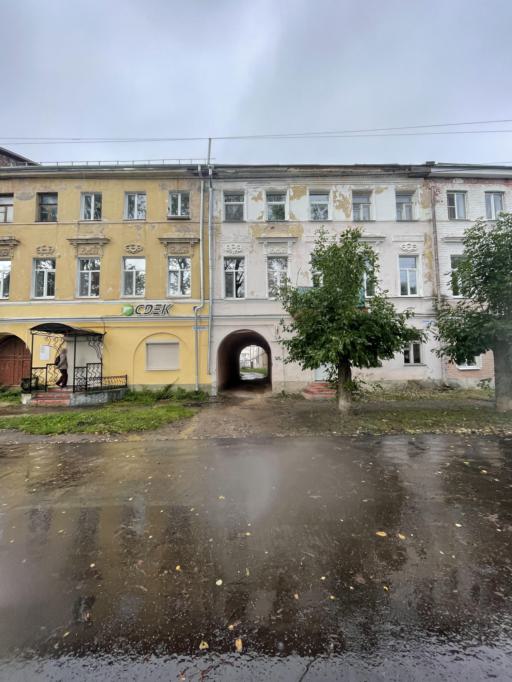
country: RU
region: Tverskaya
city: Vyshniy Volochek
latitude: 57.5848
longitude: 34.5554
